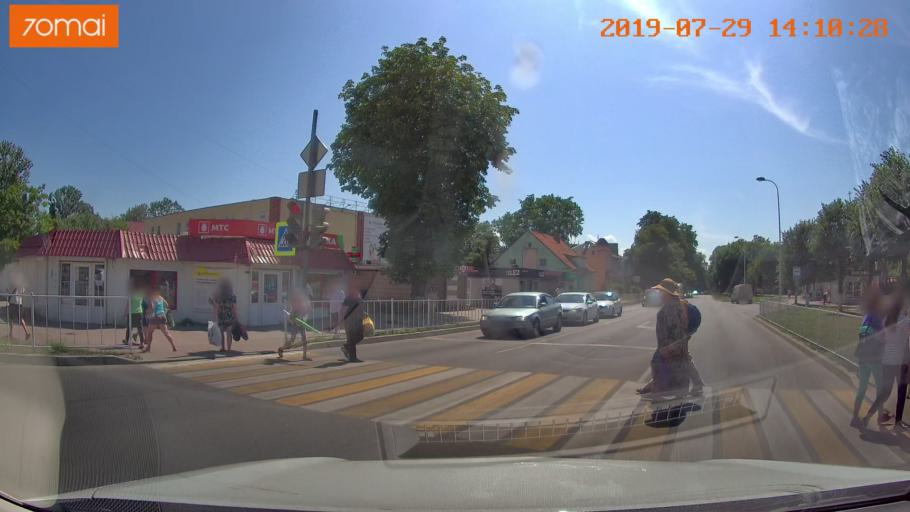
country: RU
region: Kaliningrad
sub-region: Gorod Kaliningrad
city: Baltiysk
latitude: 54.6547
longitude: 19.9116
